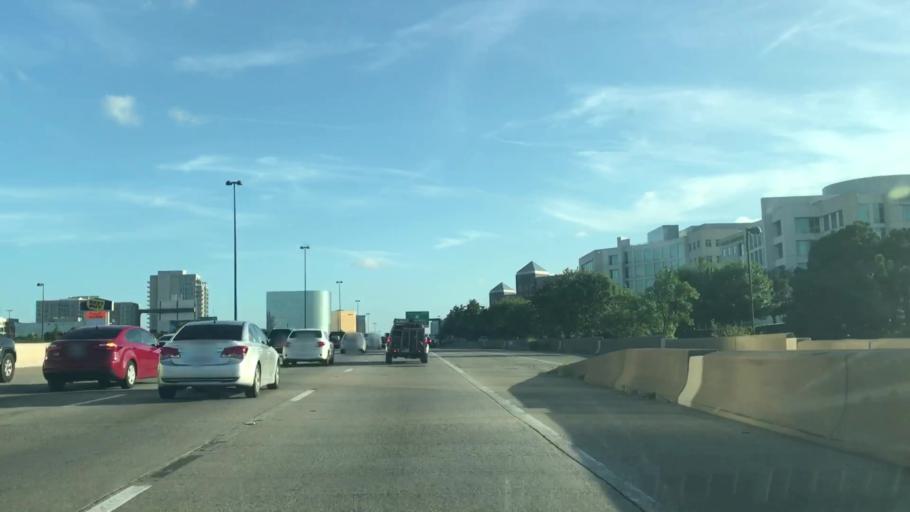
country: US
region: Texas
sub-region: Dallas County
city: University Park
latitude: 32.8770
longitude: -96.7704
